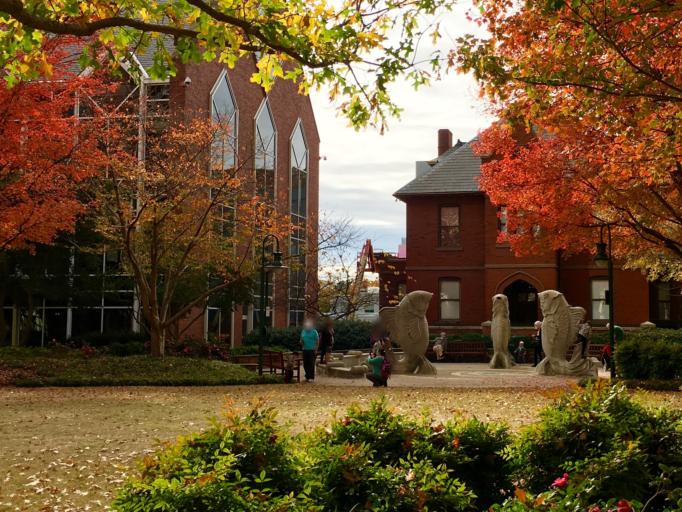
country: US
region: North Carolina
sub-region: Mecklenburg County
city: Charlotte
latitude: 35.2240
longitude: -80.8466
